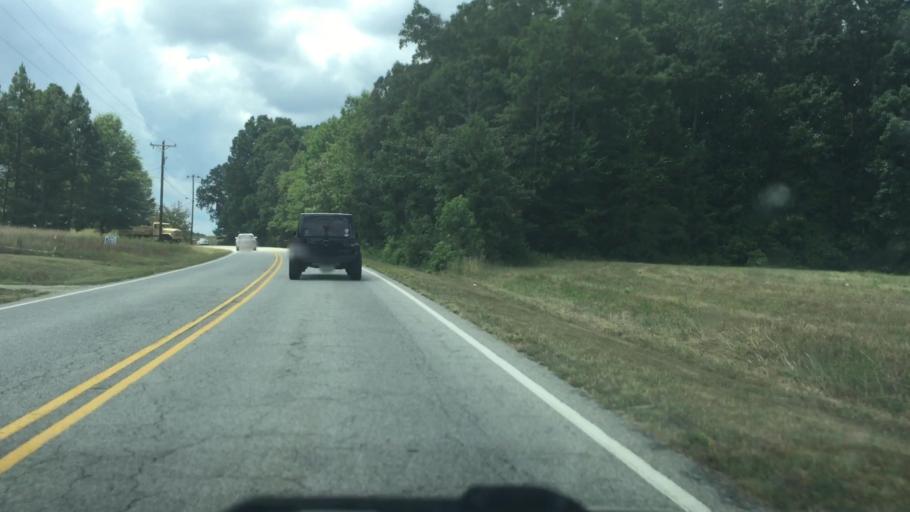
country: US
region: North Carolina
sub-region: Rowan County
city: Enochville
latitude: 35.5812
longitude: -80.6547
